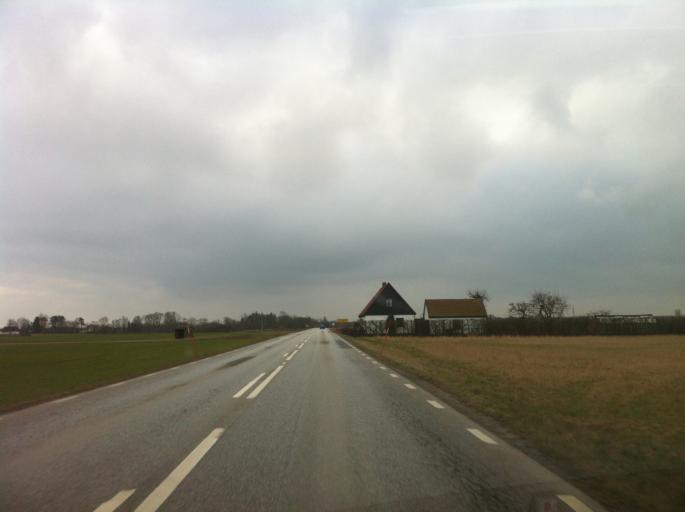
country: SE
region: Skane
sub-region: Landskrona
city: Asmundtorp
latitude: 55.8540
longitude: 12.9715
